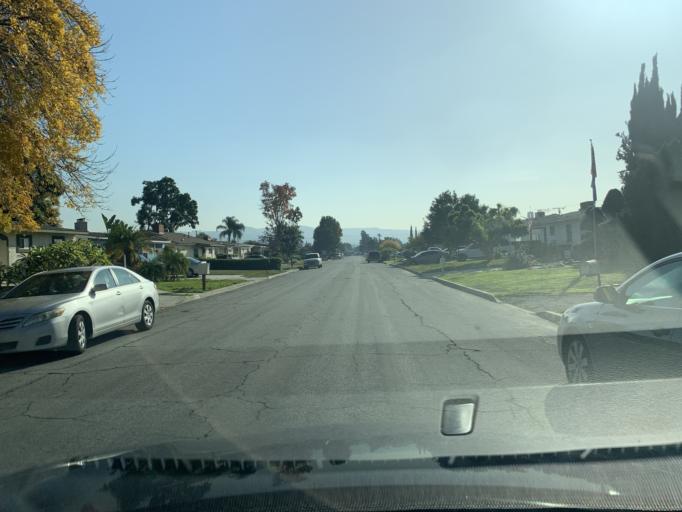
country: US
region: California
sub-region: Los Angeles County
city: Covina
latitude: 34.0782
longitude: -117.8940
